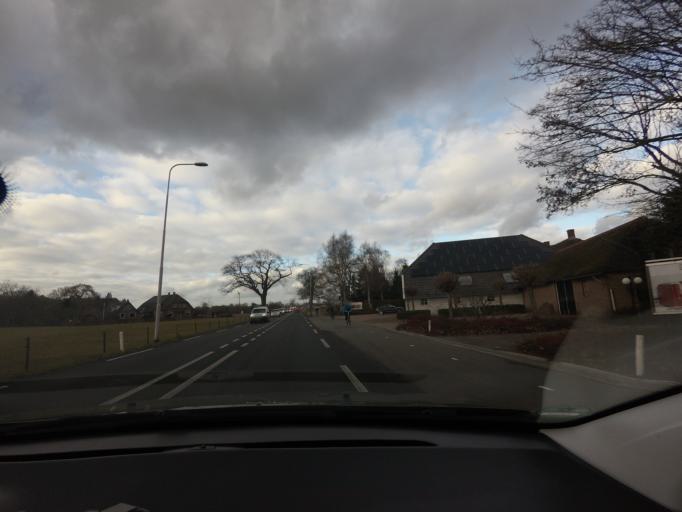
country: NL
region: Gelderland
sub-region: Gemeente Lochem
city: Epse
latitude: 52.2240
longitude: 6.1935
